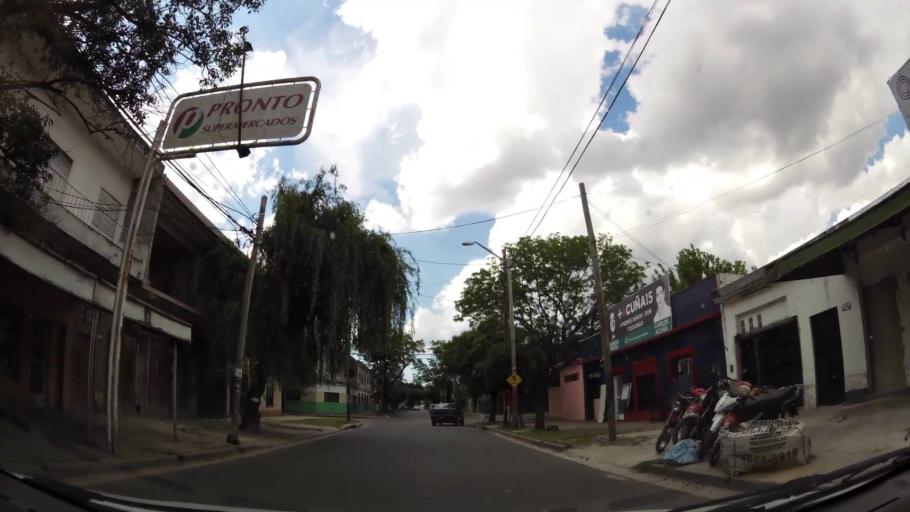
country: AR
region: Buenos Aires
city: Ituzaingo
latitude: -34.6431
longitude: -58.6632
